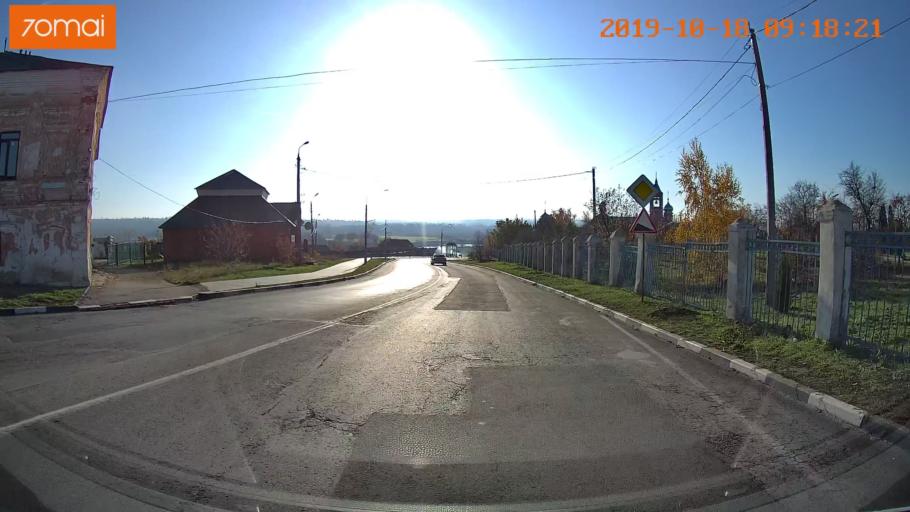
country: RU
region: Tula
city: Yefremov
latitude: 53.1374
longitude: 38.1194
